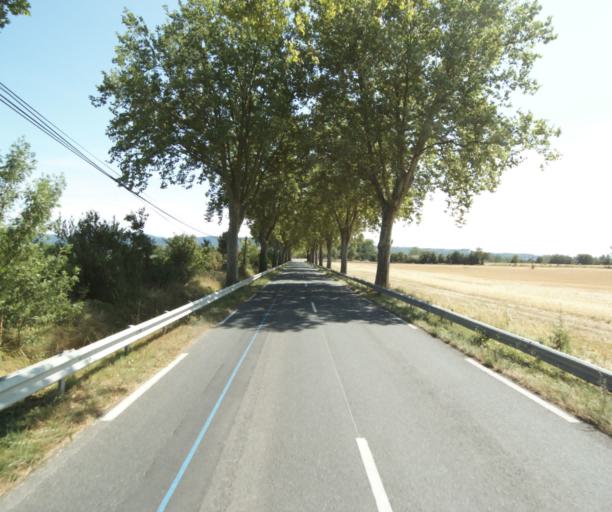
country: FR
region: Midi-Pyrenees
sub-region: Departement de la Haute-Garonne
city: Revel
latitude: 43.4808
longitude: 2.0145
